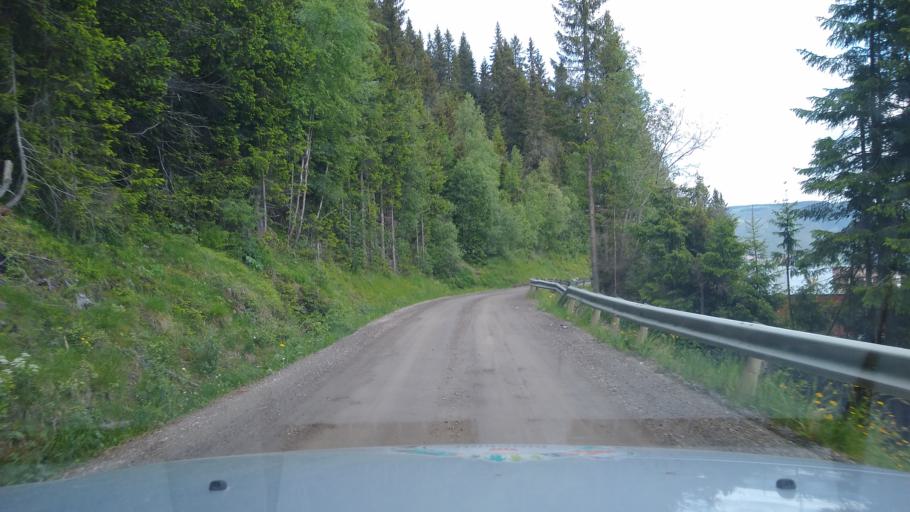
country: NO
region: Oppland
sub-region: Ringebu
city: Ringebu
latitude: 61.4995
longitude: 10.1412
